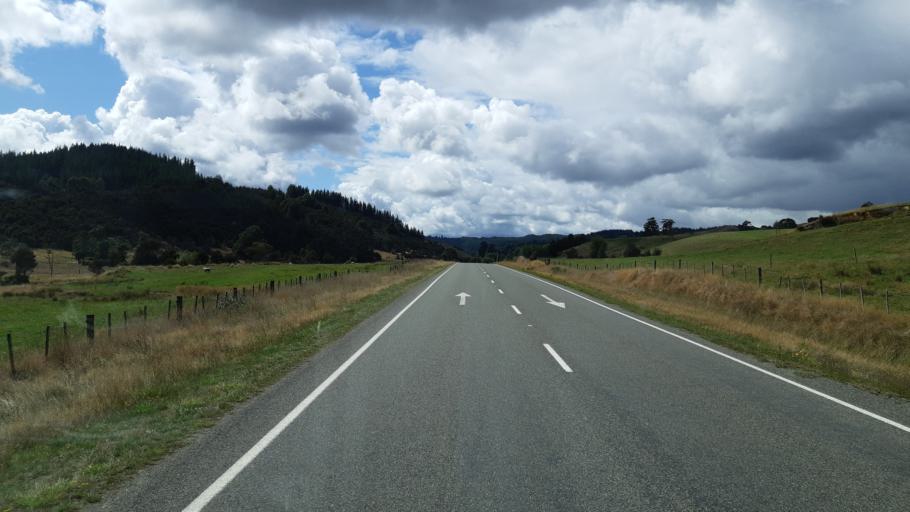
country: NZ
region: Tasman
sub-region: Tasman District
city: Wakefield
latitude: -41.6419
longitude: 172.6627
